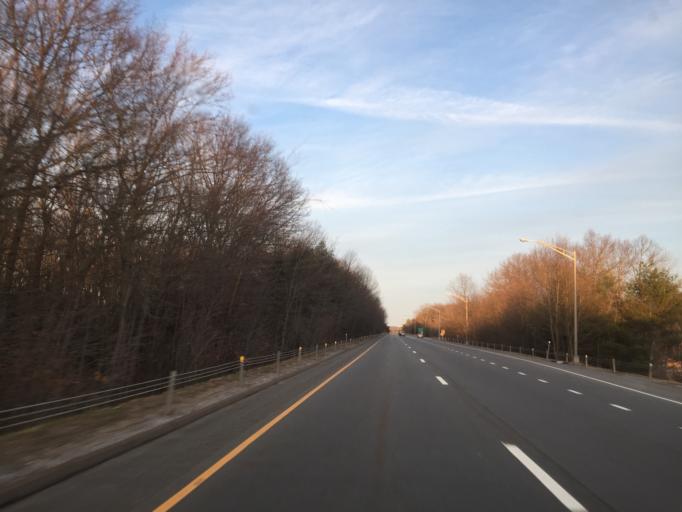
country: US
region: Connecticut
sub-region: Windham County
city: Willimantic
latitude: 41.7295
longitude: -72.2229
